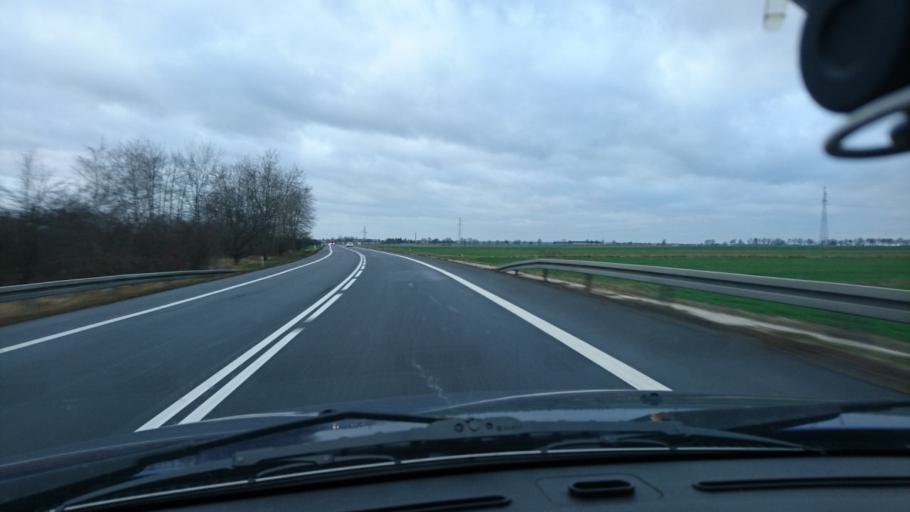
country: PL
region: Opole Voivodeship
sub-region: Powiat kluczborski
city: Kluczbork
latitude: 50.9892
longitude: 18.2328
